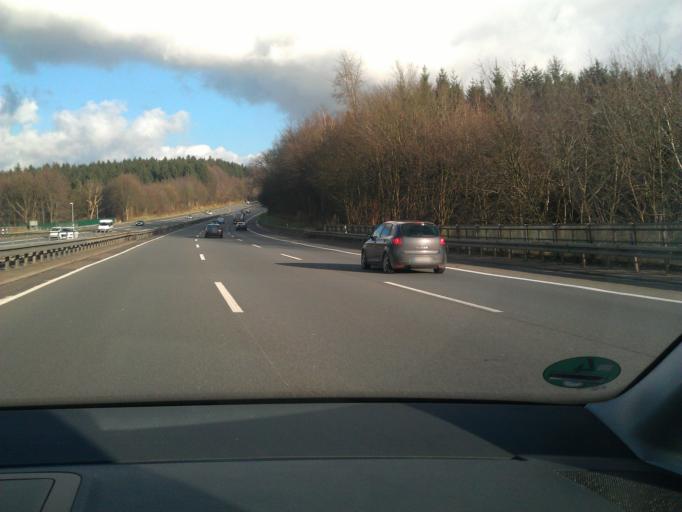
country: DE
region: North Rhine-Westphalia
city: Burscheid
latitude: 51.1173
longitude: 7.1529
